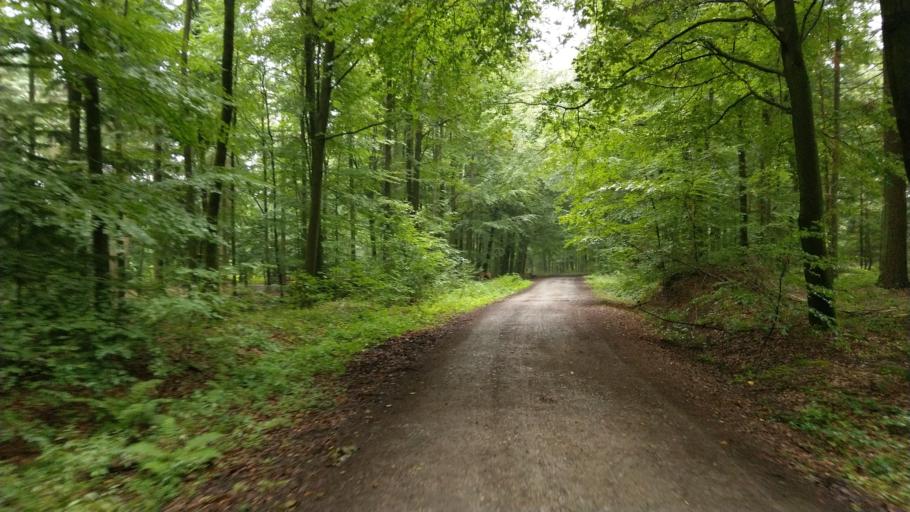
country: NL
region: Limburg
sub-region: Gemeente Vaals
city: Vaals
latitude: 50.7453
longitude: 6.0343
